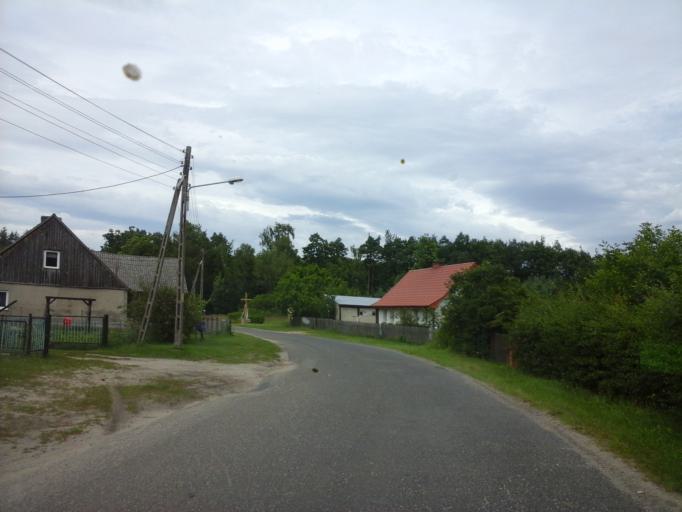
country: PL
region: Lubusz
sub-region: Powiat strzelecko-drezdenecki
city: Dobiegniew
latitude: 53.0910
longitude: 15.7838
